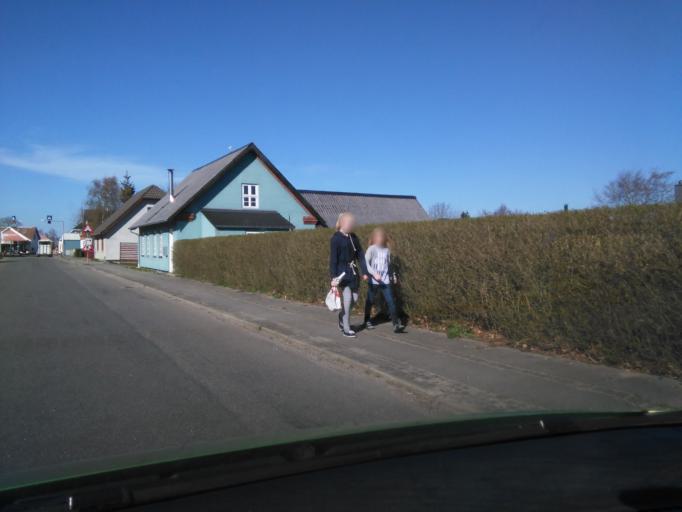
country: DK
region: South Denmark
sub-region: Varde Kommune
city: Oksbol
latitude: 55.6541
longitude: 8.2905
